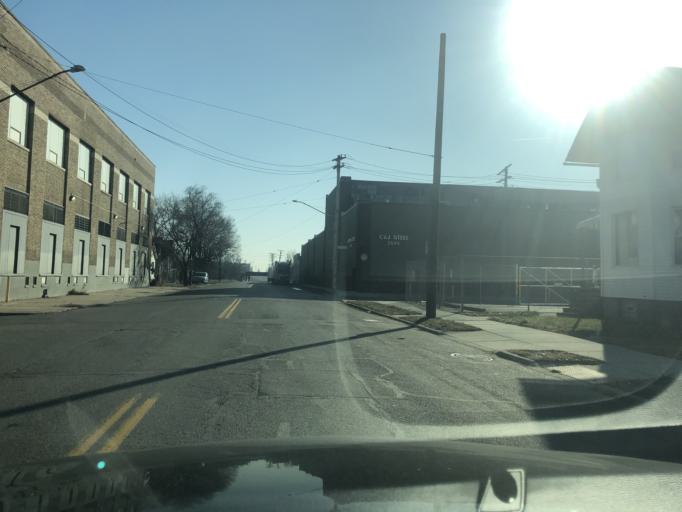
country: US
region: Michigan
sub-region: Wayne County
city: Detroit
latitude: 42.3346
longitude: -83.1037
